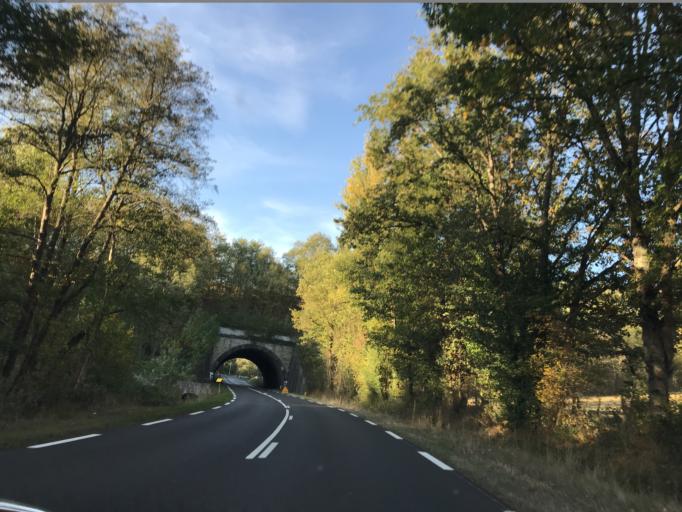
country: FR
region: Auvergne
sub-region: Departement du Puy-de-Dome
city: Paslieres
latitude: 45.8861
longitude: 3.5229
